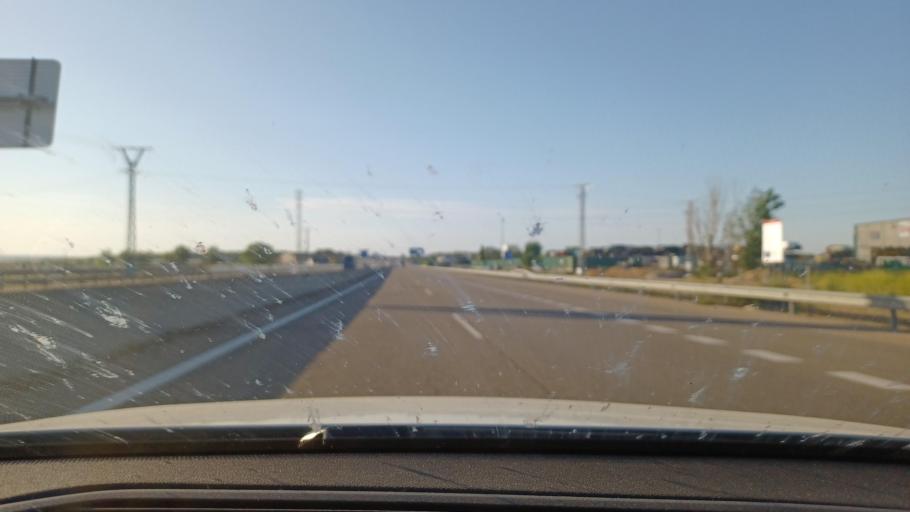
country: ES
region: Castille and Leon
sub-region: Provincia de Valladolid
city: Cisterniga
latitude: 41.5975
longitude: -4.6966
